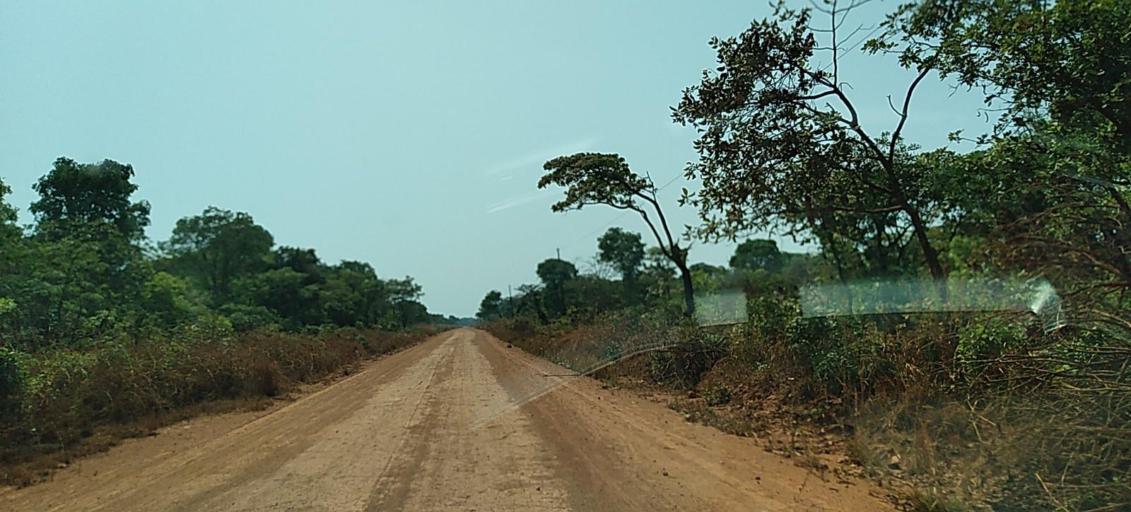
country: ZM
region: North-Western
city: Kansanshi
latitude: -11.9934
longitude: 26.6336
